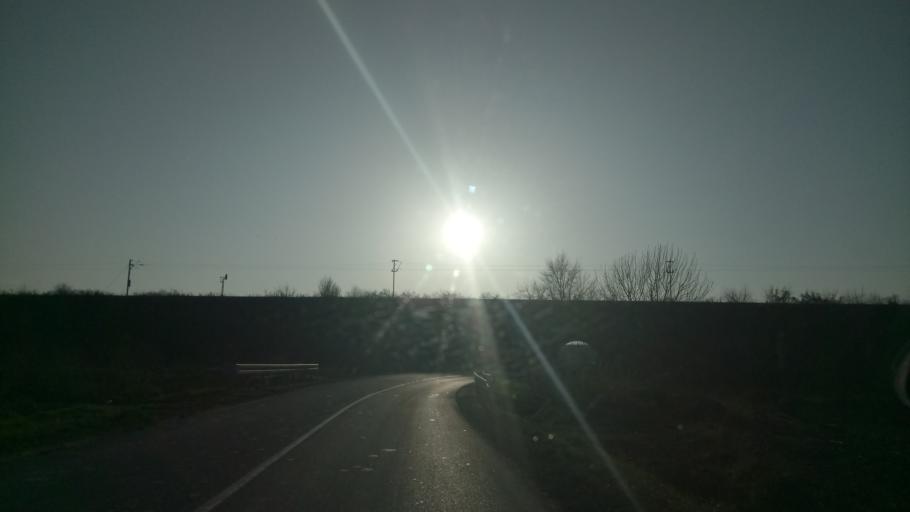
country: RS
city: Beska
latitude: 45.1215
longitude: 20.0606
